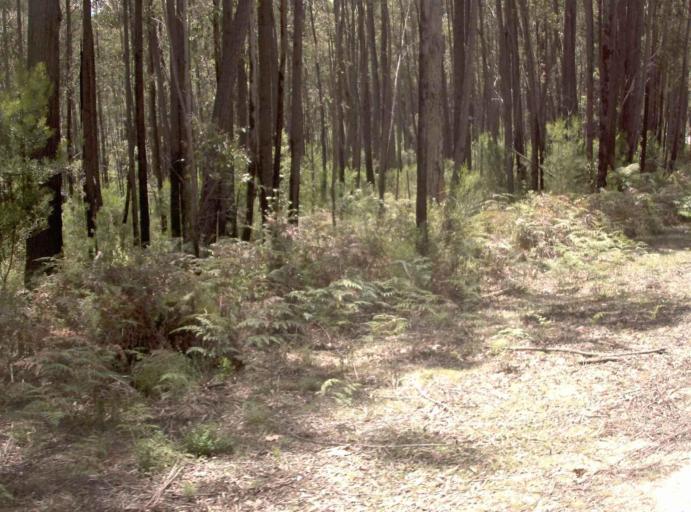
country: AU
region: New South Wales
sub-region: Bombala
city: Bombala
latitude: -37.5642
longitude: 148.9458
